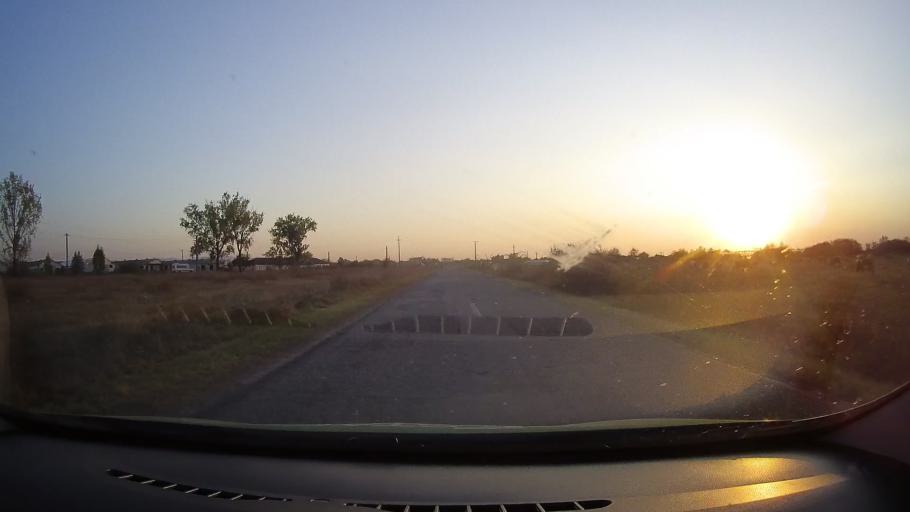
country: RO
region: Arad
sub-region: Comuna Seleus
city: Seleus
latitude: 46.3905
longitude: 21.7116
